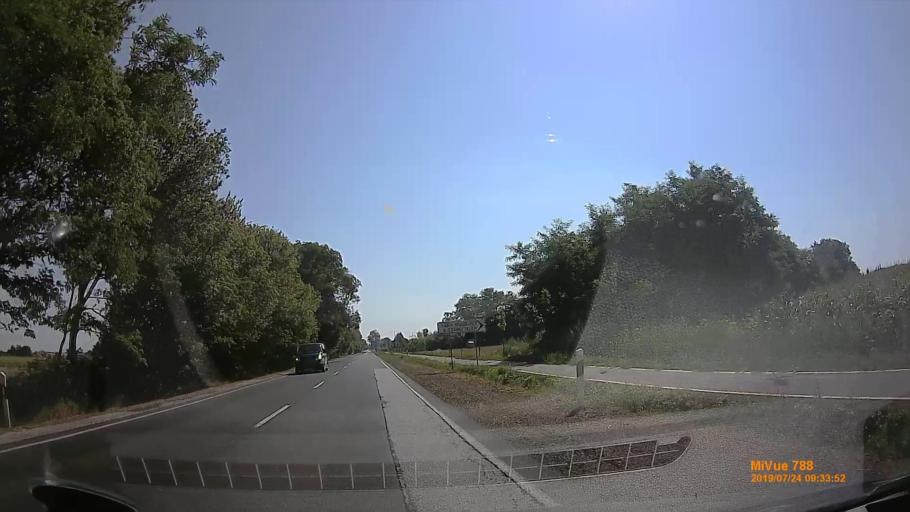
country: HU
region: Szabolcs-Szatmar-Bereg
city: Napkor
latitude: 47.9516
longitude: 21.8574
